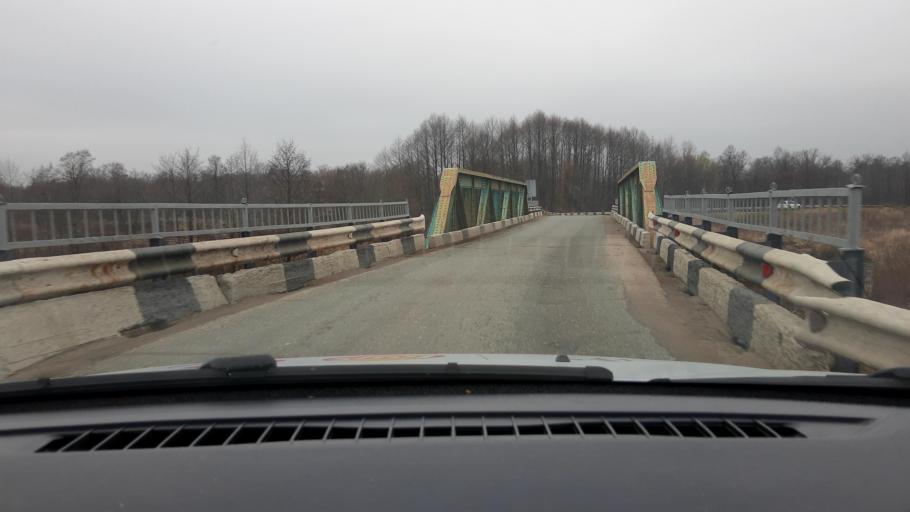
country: RU
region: Nizjnij Novgorod
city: Neklyudovo
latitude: 56.4228
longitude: 43.9254
